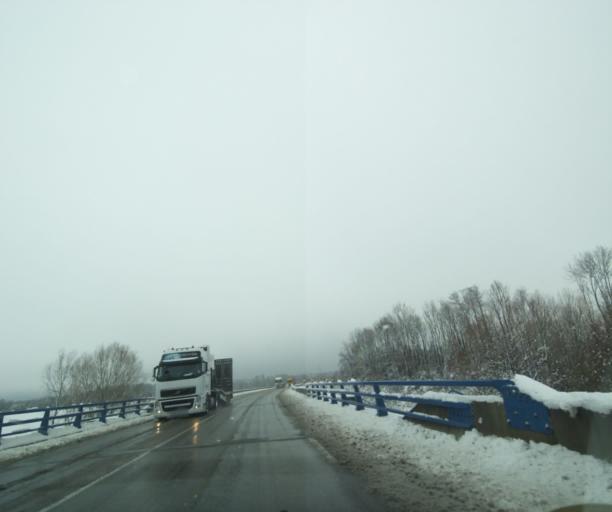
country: FR
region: Champagne-Ardenne
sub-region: Departement de la Haute-Marne
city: Saint-Dizier
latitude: 48.5793
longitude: 4.8845
